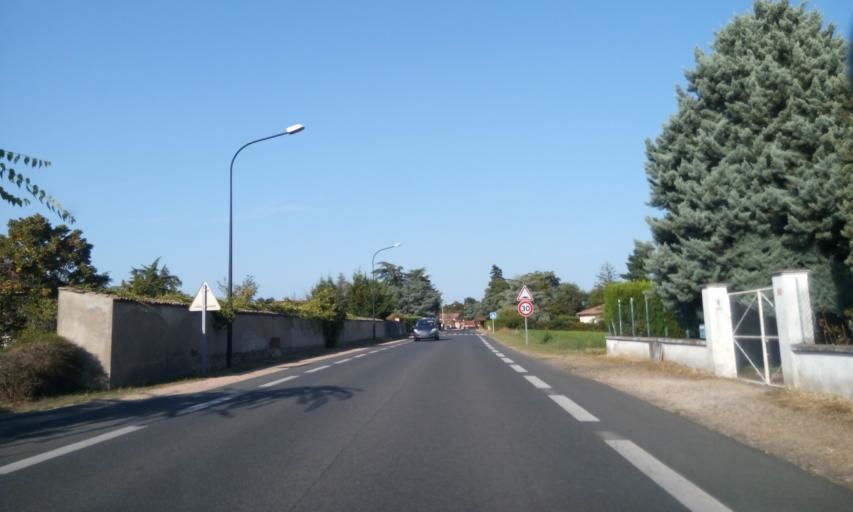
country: FR
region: Rhone-Alpes
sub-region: Departement de l'Ain
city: Trevoux
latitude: 45.9462
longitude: 4.7394
